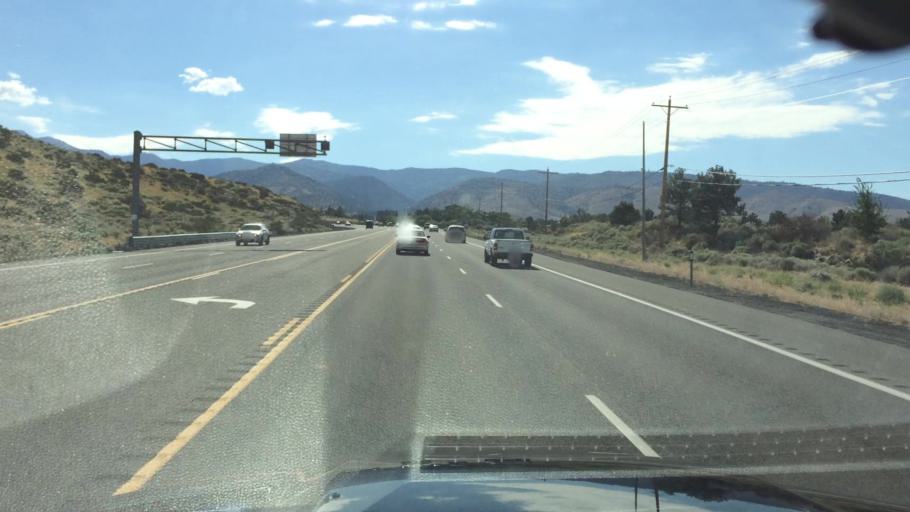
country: US
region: Nevada
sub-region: Washoe County
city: Reno
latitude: 39.3919
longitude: -119.7930
